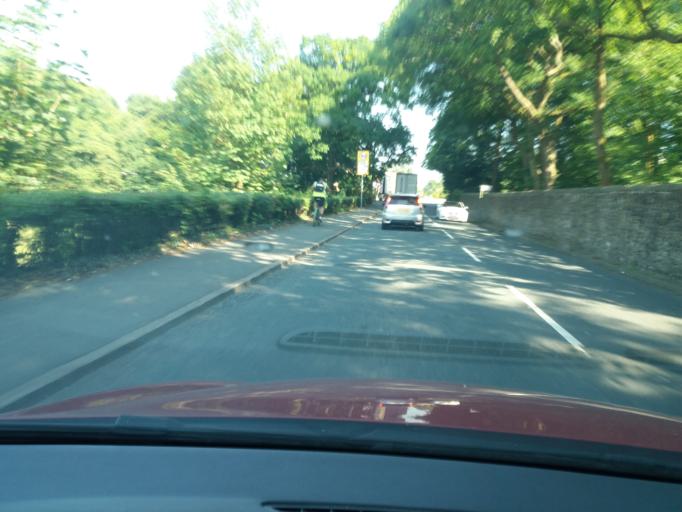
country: GB
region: England
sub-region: Lancashire
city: Clayton-le-Woods
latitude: 53.6849
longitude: -2.6407
